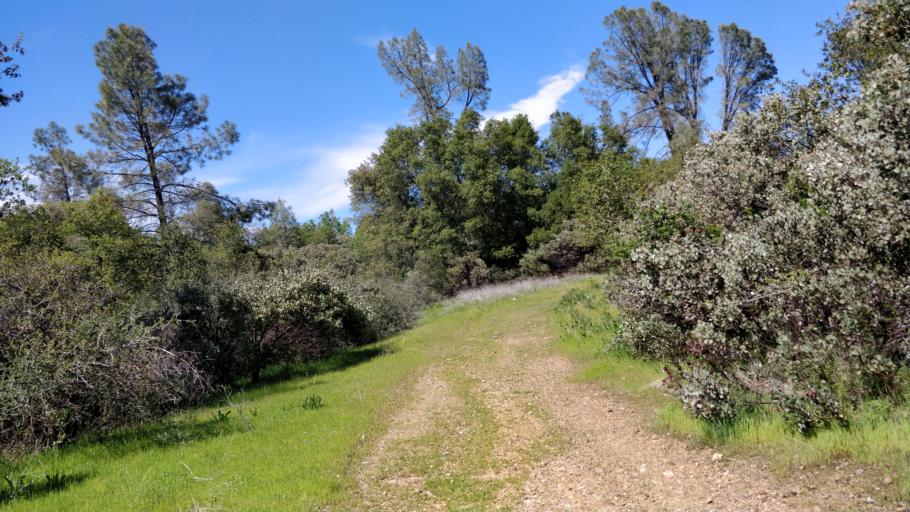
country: US
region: California
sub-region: Shasta County
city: Shasta Lake
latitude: 40.6705
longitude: -122.3560
